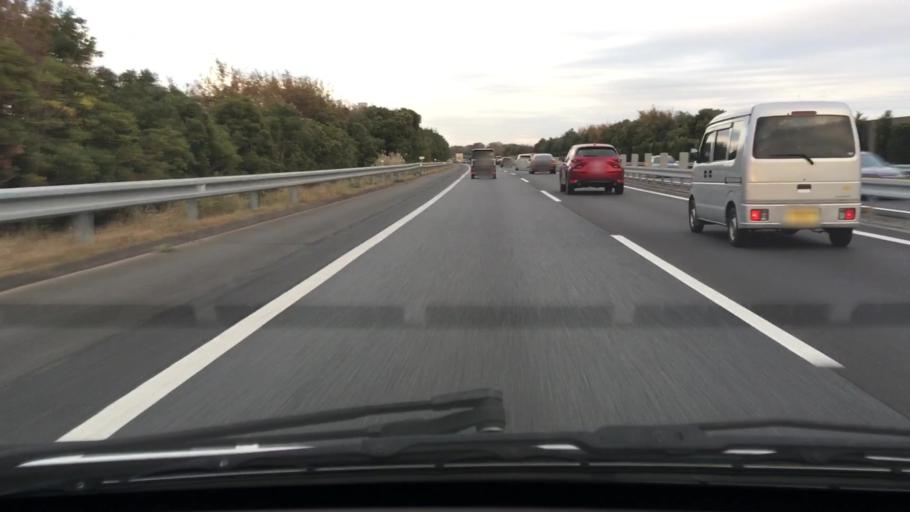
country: JP
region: Chiba
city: Ichihara
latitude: 35.5115
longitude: 140.1127
